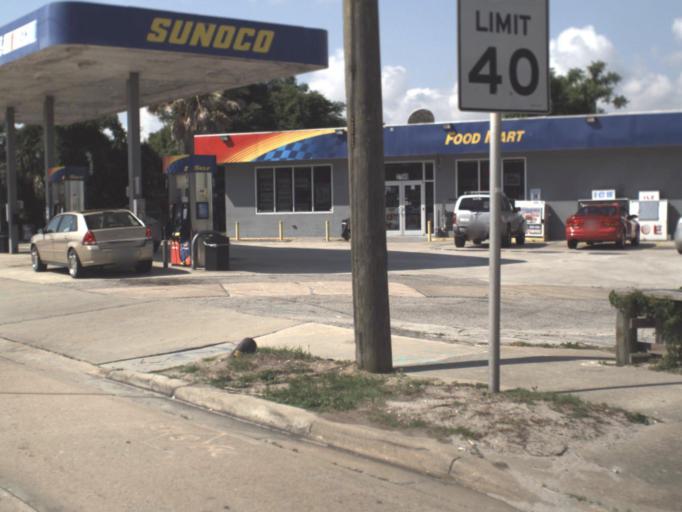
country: US
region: Florida
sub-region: Saint Johns County
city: Saint Augustine
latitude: 29.9129
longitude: -81.3232
